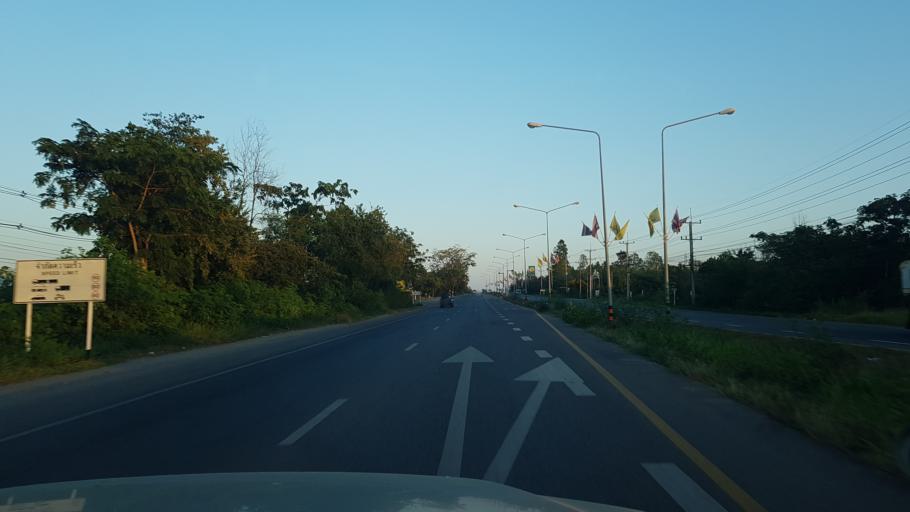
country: TH
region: Khon Kaen
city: Chum Phae
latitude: 16.5778
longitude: 102.0251
